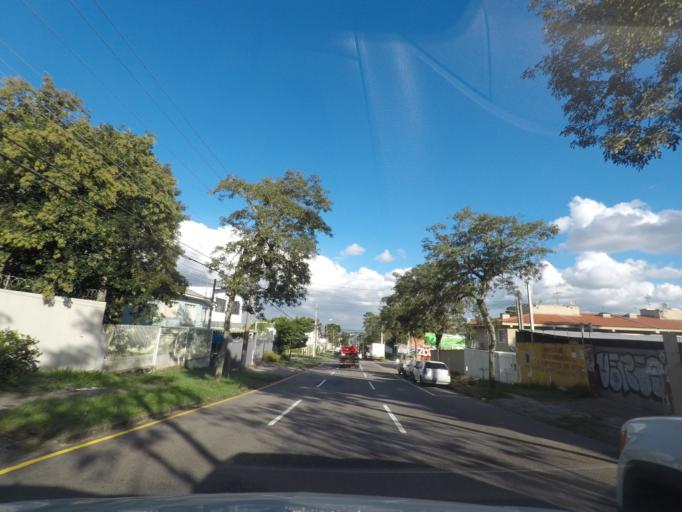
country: BR
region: Parana
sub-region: Curitiba
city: Curitiba
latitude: -25.4607
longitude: -49.2598
